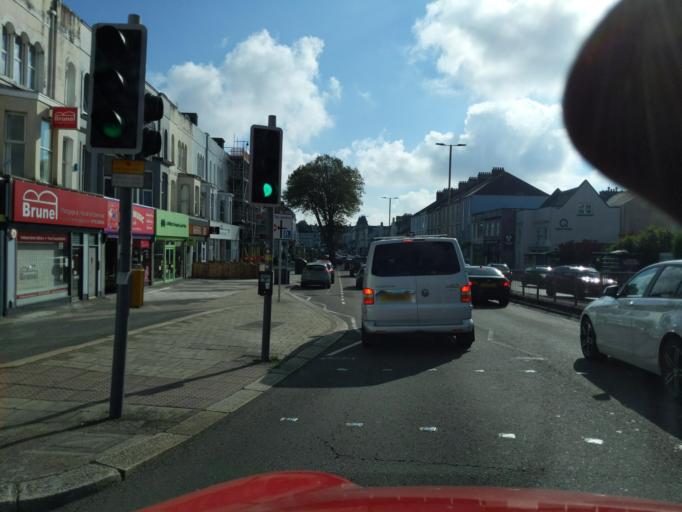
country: GB
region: England
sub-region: Plymouth
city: Plymouth
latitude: 50.3839
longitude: -4.1344
